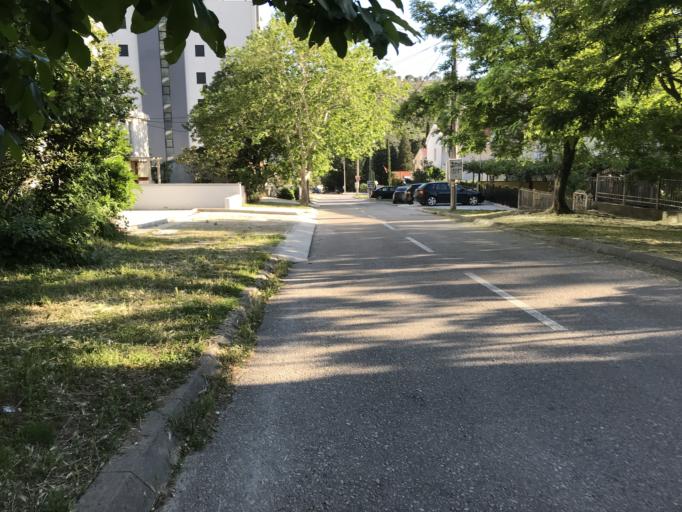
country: ME
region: Bar
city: Sutomore
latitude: 42.1411
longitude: 19.0458
